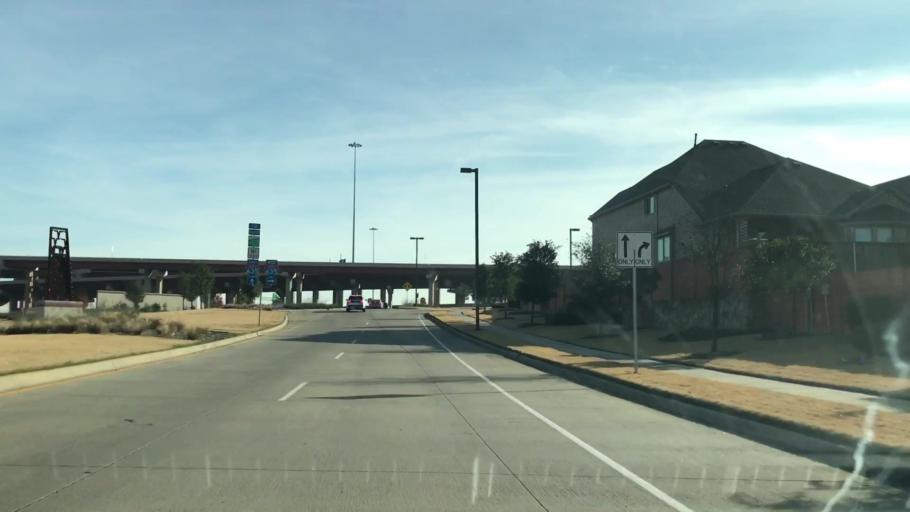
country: US
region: Texas
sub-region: Dallas County
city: Farmers Branch
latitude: 32.9148
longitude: -96.9439
